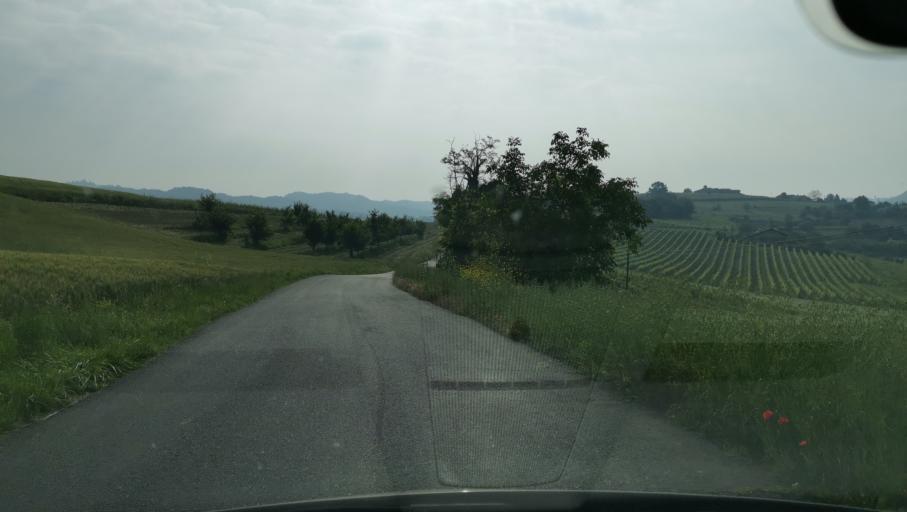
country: IT
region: Piedmont
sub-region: Provincia di Alessandria
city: Odalengo Piccolo
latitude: 45.0701
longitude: 8.2198
